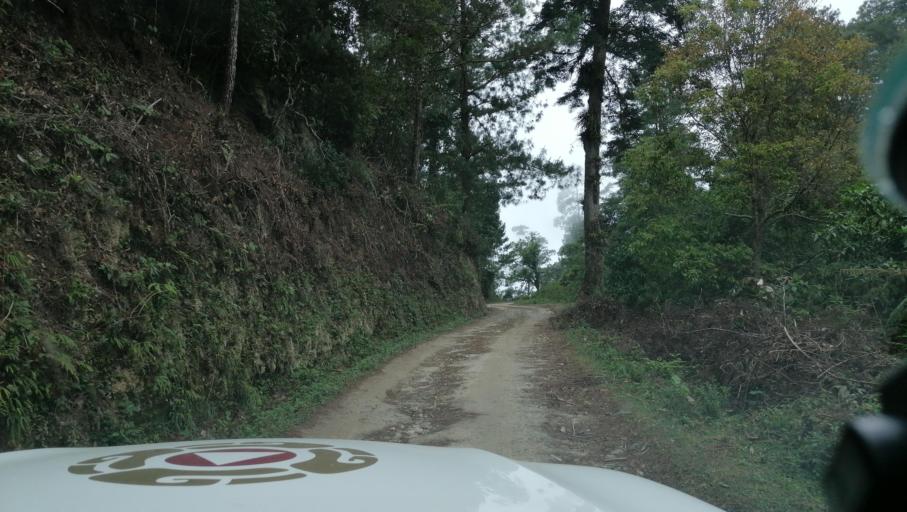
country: MX
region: Chiapas
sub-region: Tapachula
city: Canton Villaflor
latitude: 15.1983
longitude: -92.2328
